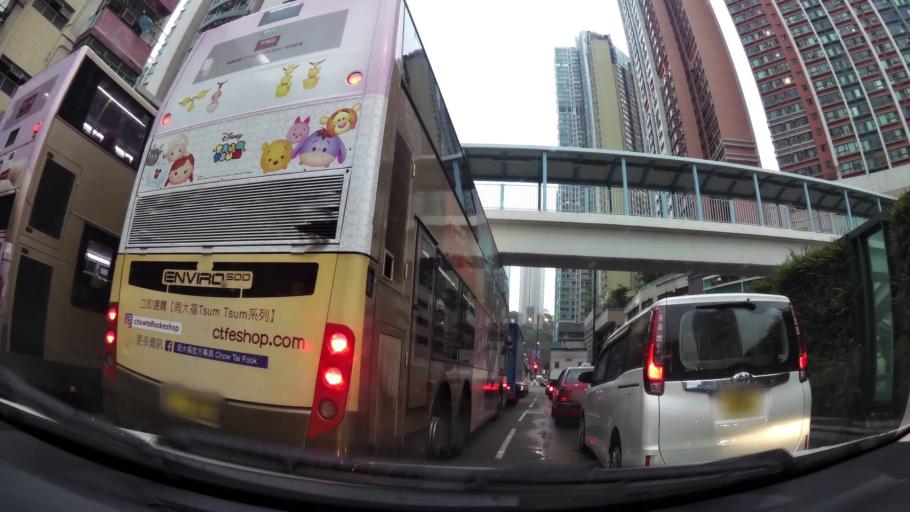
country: HK
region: Tsuen Wan
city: Tsuen Wan
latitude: 22.3676
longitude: 114.1165
